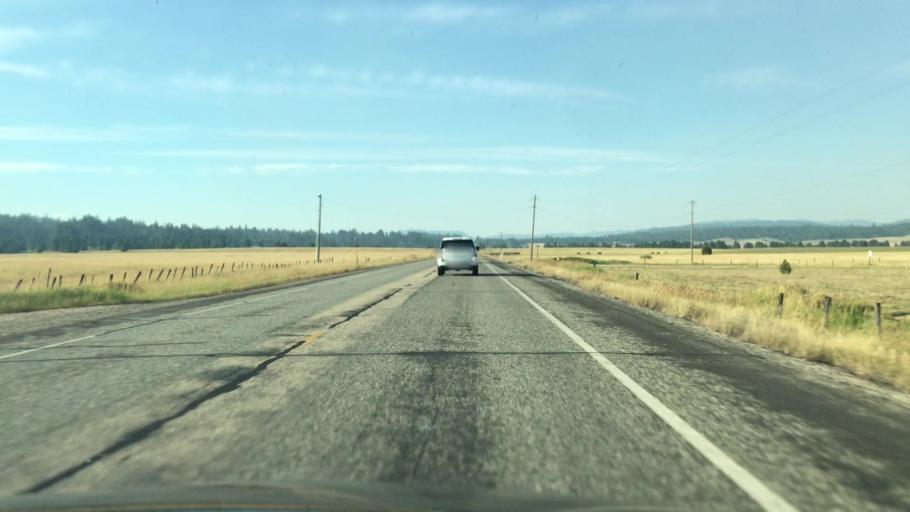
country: US
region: Idaho
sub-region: Valley County
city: Cascade
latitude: 44.3434
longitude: -116.0282
